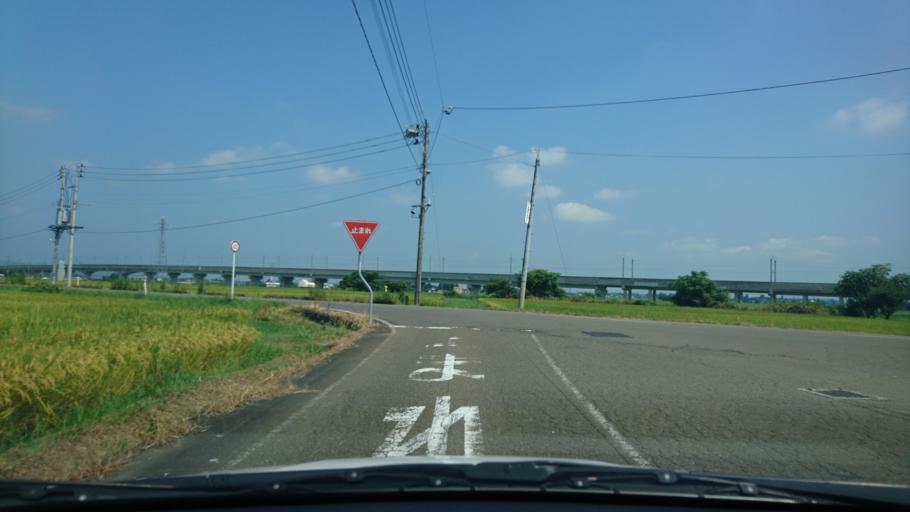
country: JP
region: Niigata
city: Arai
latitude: 37.0630
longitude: 138.2666
